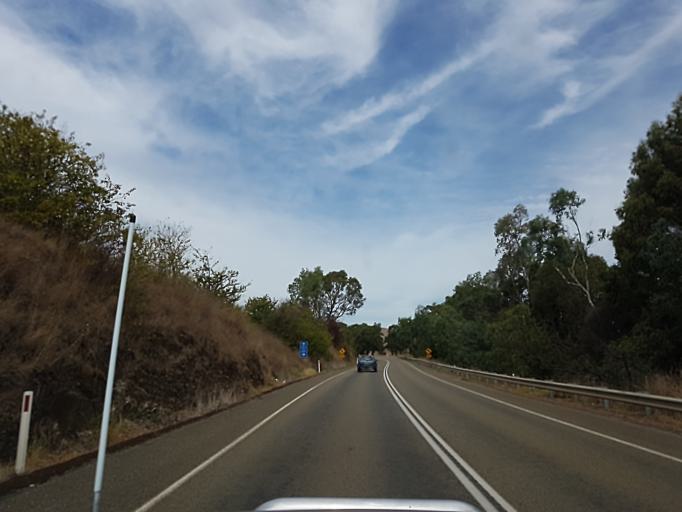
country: AU
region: Victoria
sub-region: Murrindindi
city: Alexandra
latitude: -37.2106
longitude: 145.4368
